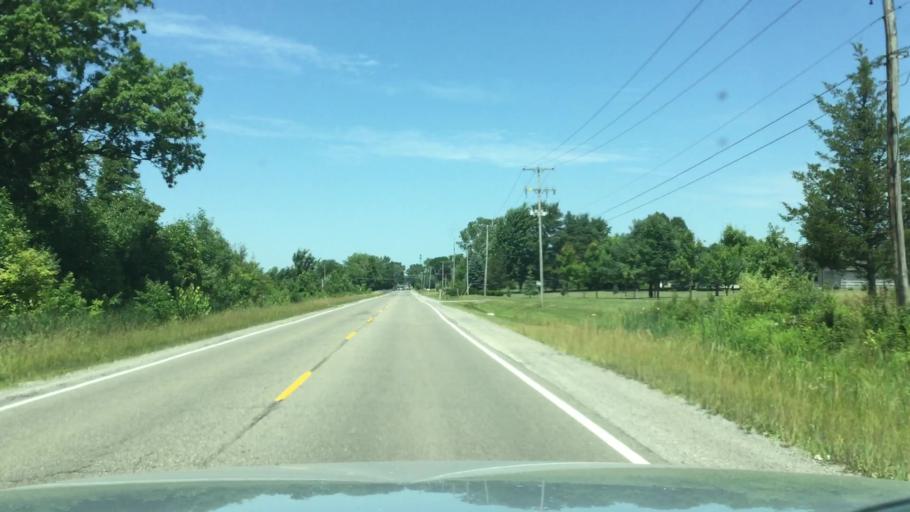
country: US
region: Michigan
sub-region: Genesee County
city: Swartz Creek
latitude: 42.9509
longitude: -83.8109
